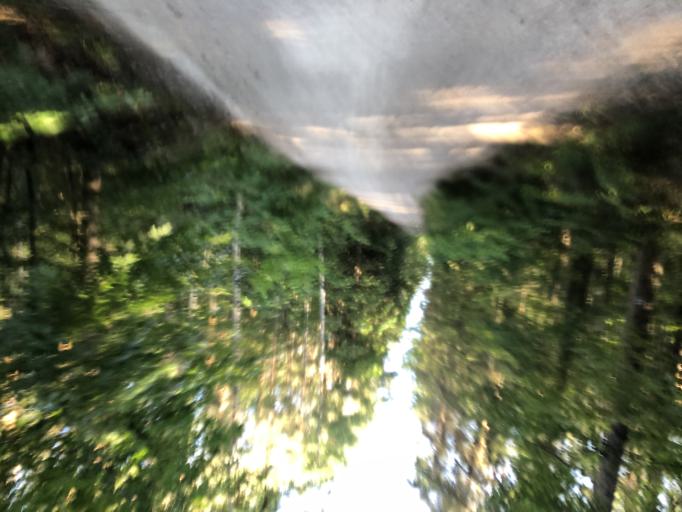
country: DE
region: Bavaria
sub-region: Regierungsbezirk Mittelfranken
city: Kalchreuth
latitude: 49.5489
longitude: 11.1005
